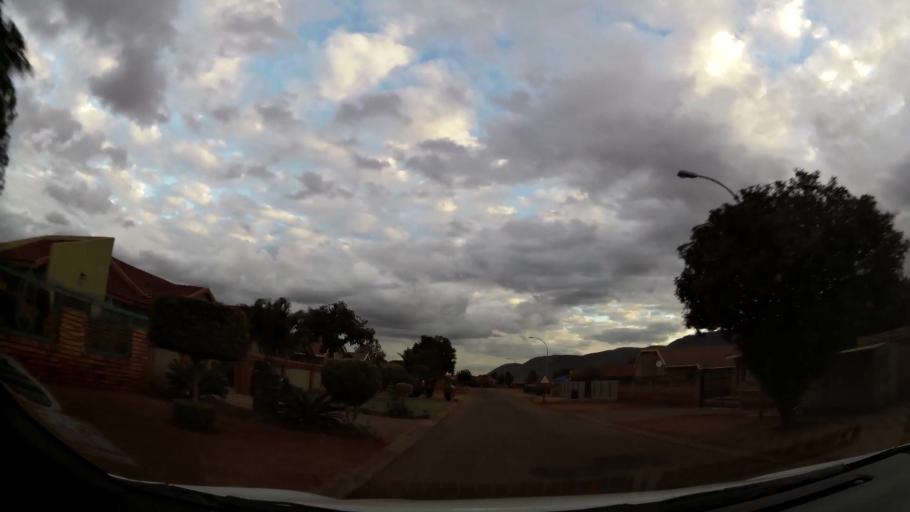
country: ZA
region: Limpopo
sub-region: Waterberg District Municipality
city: Mokopane
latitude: -24.1981
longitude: 28.9896
